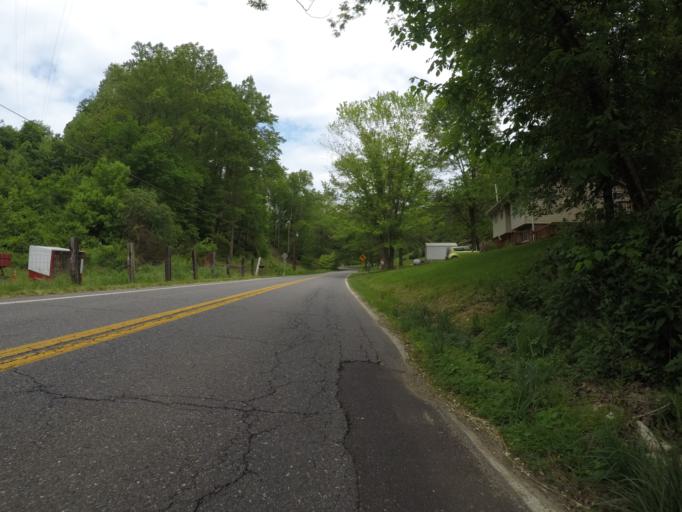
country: US
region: West Virginia
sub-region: Wayne County
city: Ceredo
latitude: 38.3535
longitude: -82.5462
